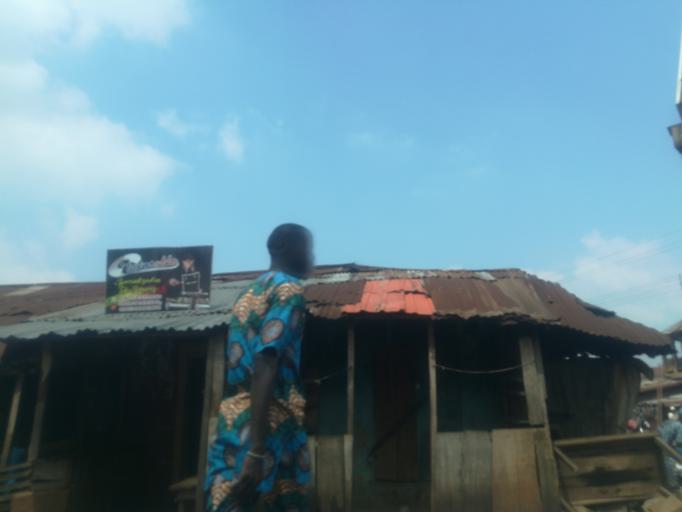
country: NG
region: Oyo
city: Ibadan
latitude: 7.3915
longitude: 3.9071
